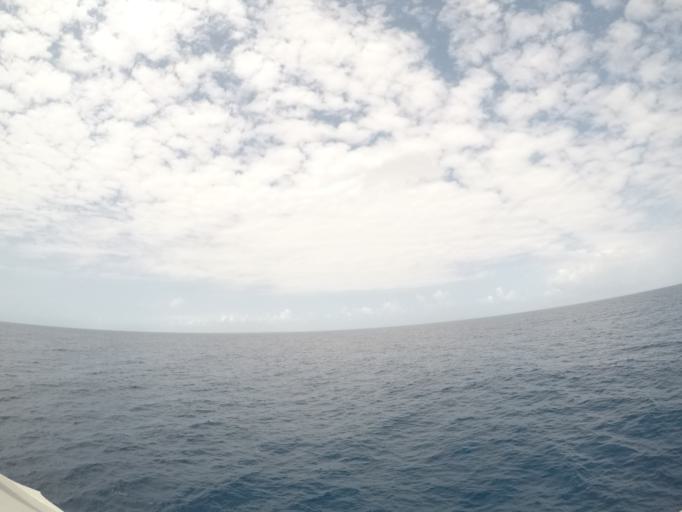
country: TZ
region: Zanzibar North
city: Nungwi
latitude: -5.6000
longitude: 39.3419
